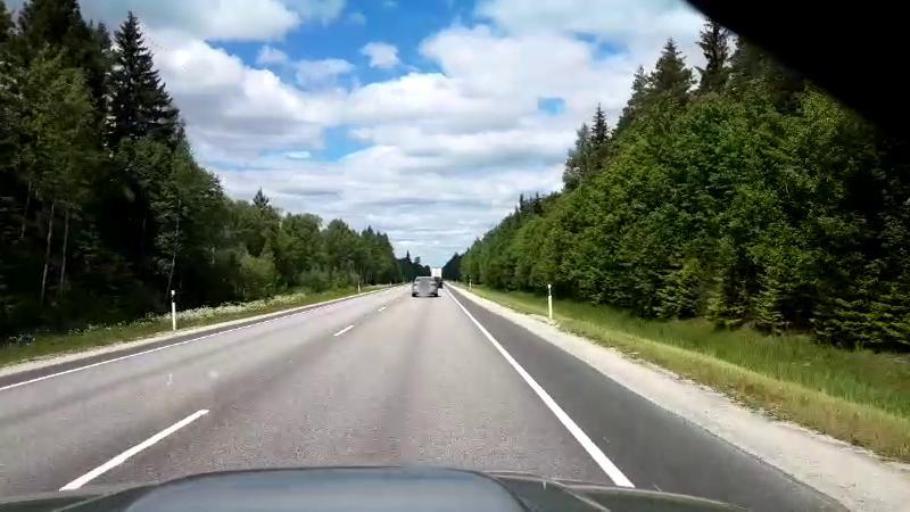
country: EE
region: Paernumaa
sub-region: Halinga vald
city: Parnu-Jaagupi
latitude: 58.7167
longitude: 24.4238
